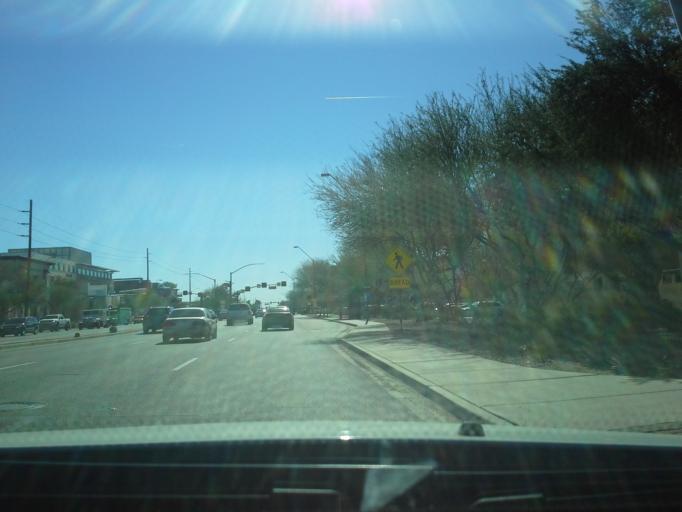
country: US
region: Arizona
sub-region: Maricopa County
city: Paradise Valley
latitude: 33.6257
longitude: -111.9257
